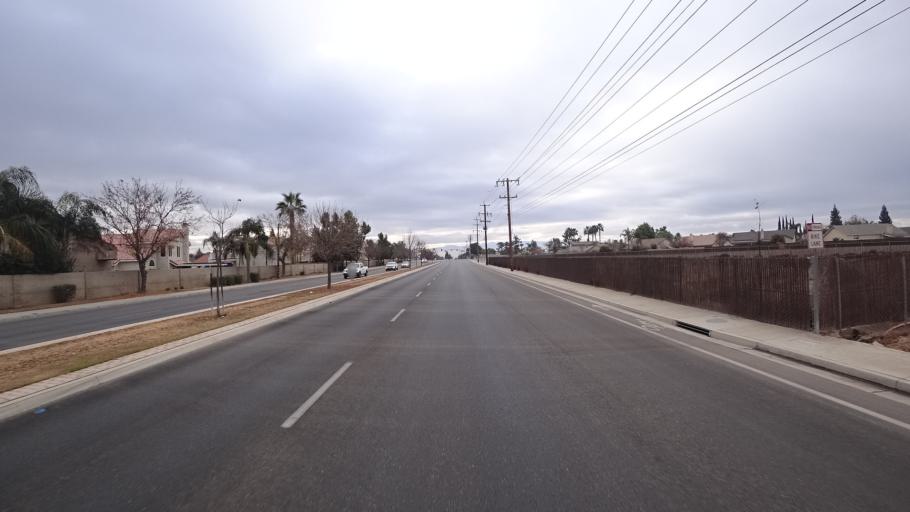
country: US
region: California
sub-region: Kern County
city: Greenfield
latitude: 35.3055
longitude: -119.0745
